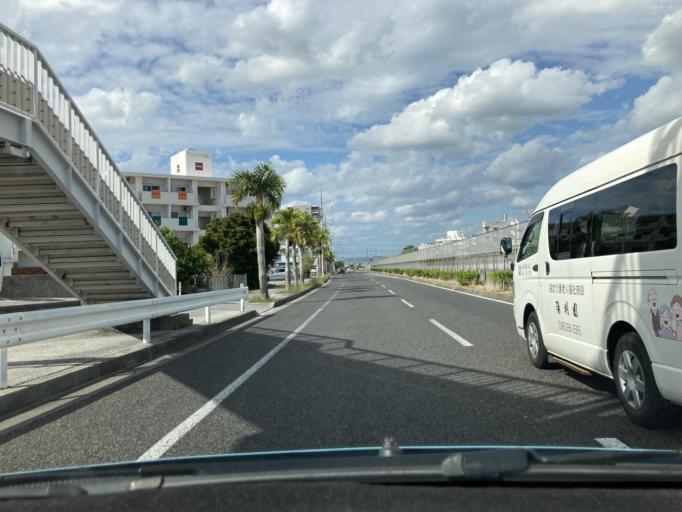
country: JP
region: Okinawa
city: Okinawa
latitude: 26.3236
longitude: 127.7883
